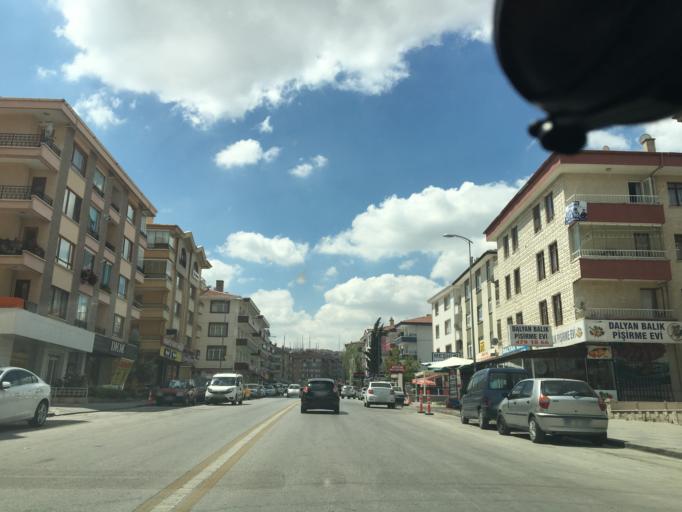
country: TR
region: Ankara
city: Ankara
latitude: 39.8873
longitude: 32.8289
